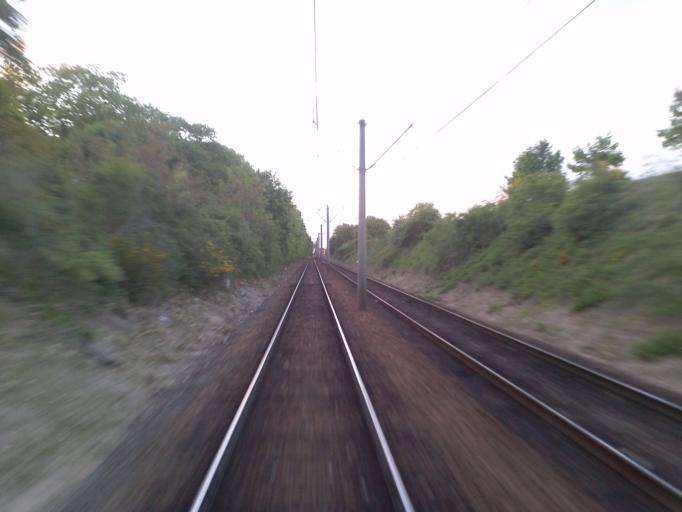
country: DE
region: Baden-Wuerttemberg
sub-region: Karlsruhe Region
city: Karlsruhe
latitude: 49.0251
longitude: 8.3759
